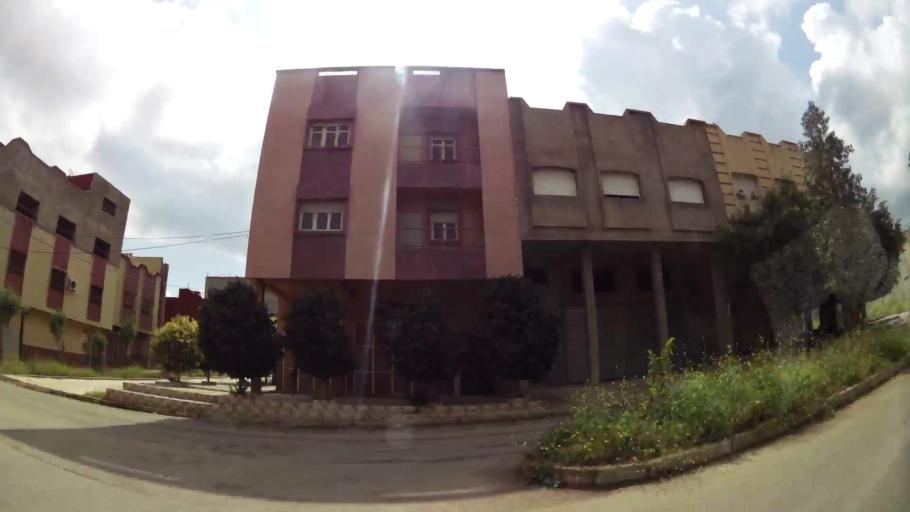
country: MA
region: Rabat-Sale-Zemmour-Zaer
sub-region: Khemisset
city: Tiflet
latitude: 33.8971
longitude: -6.3370
